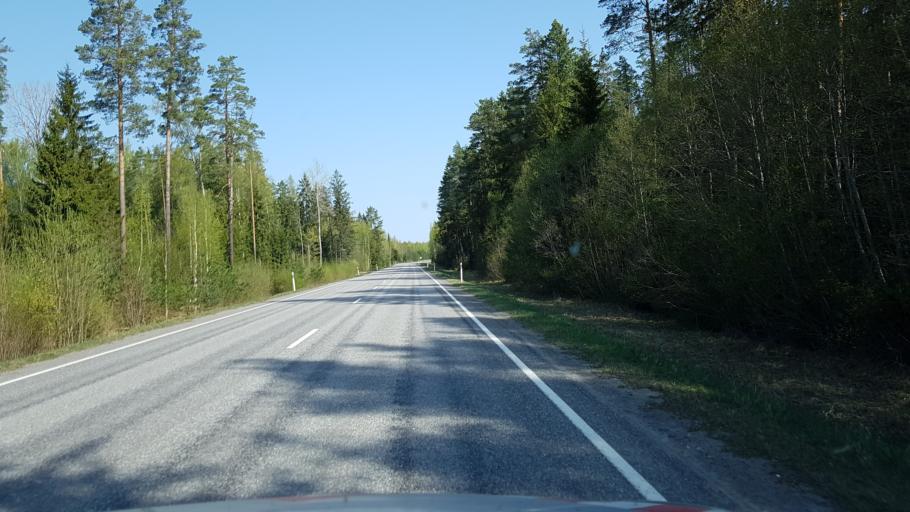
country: EE
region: Paernumaa
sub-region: Saarde vald
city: Kilingi-Nomme
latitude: 58.1867
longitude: 25.0545
